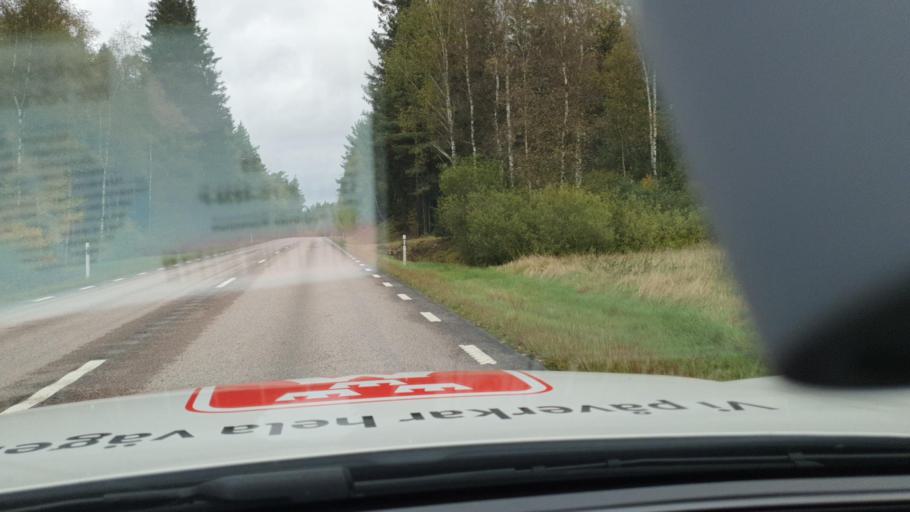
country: SE
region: Halland
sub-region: Halmstads Kommun
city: Getinge
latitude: 57.1162
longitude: 12.7754
